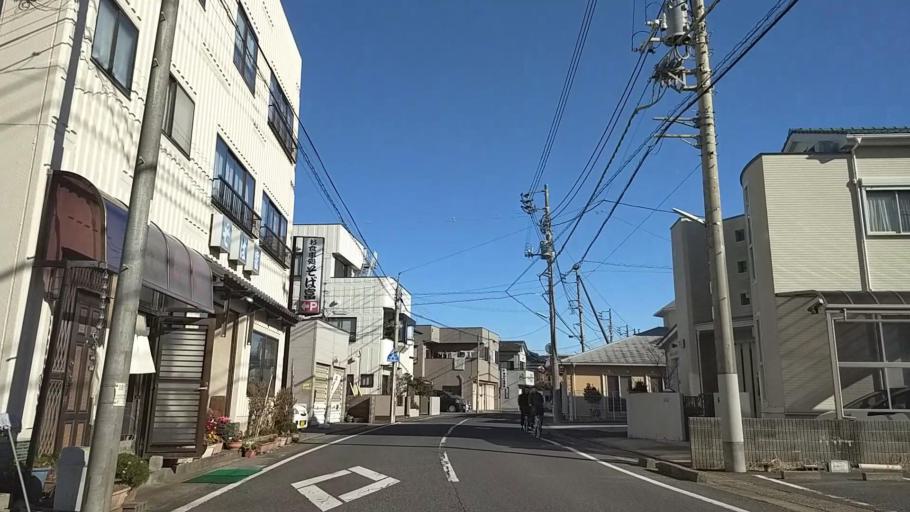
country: JP
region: Chiba
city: Hasaki
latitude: 35.7347
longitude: 140.8471
